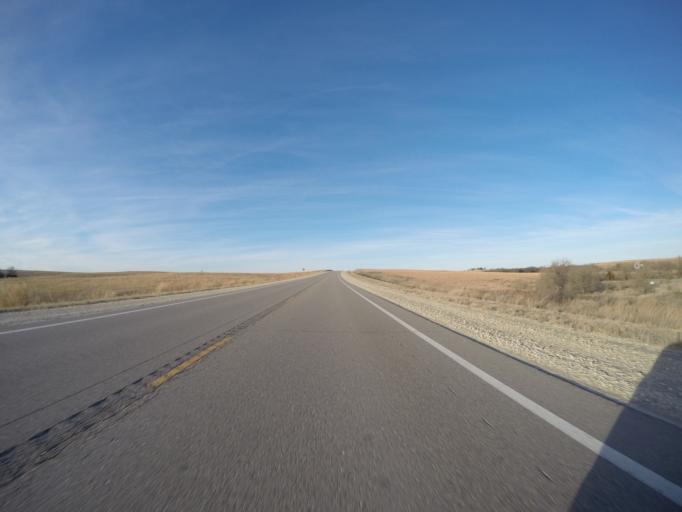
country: US
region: Kansas
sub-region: Marion County
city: Marion
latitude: 38.2956
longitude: -96.9664
